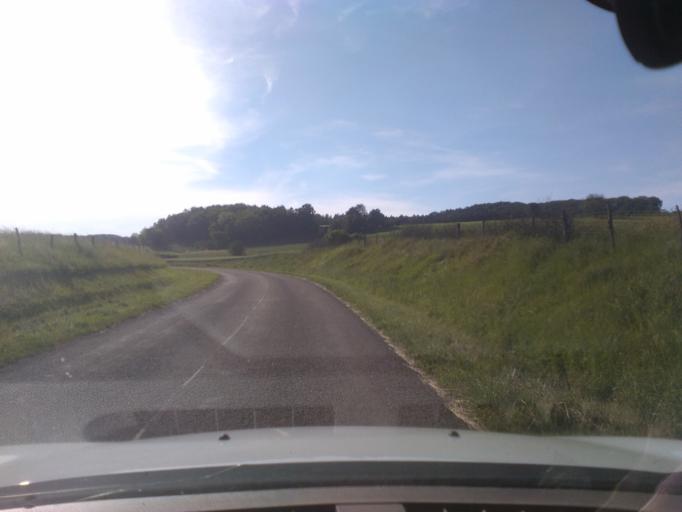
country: FR
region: Lorraine
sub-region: Departement des Vosges
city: Mirecourt
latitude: 48.2668
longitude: 6.2161
